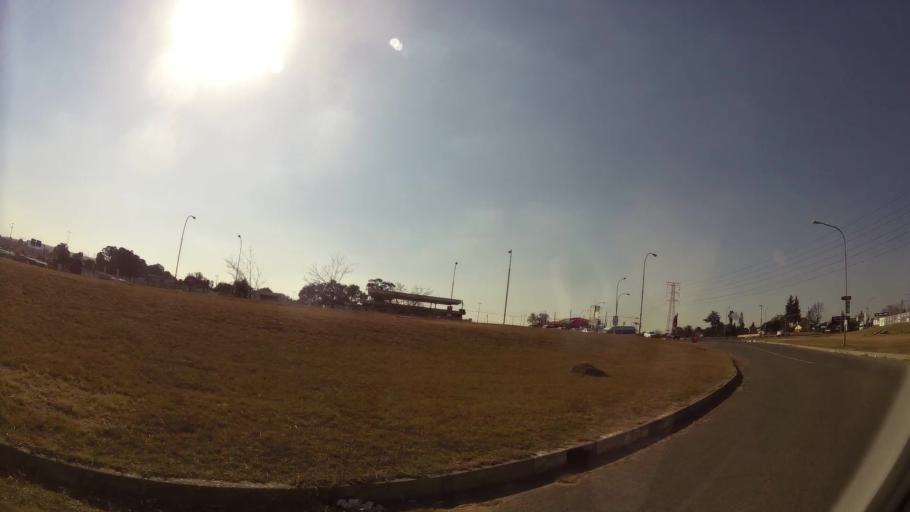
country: ZA
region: Gauteng
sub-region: City of Johannesburg Metropolitan Municipality
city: Johannesburg
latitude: -26.2583
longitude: 27.9906
